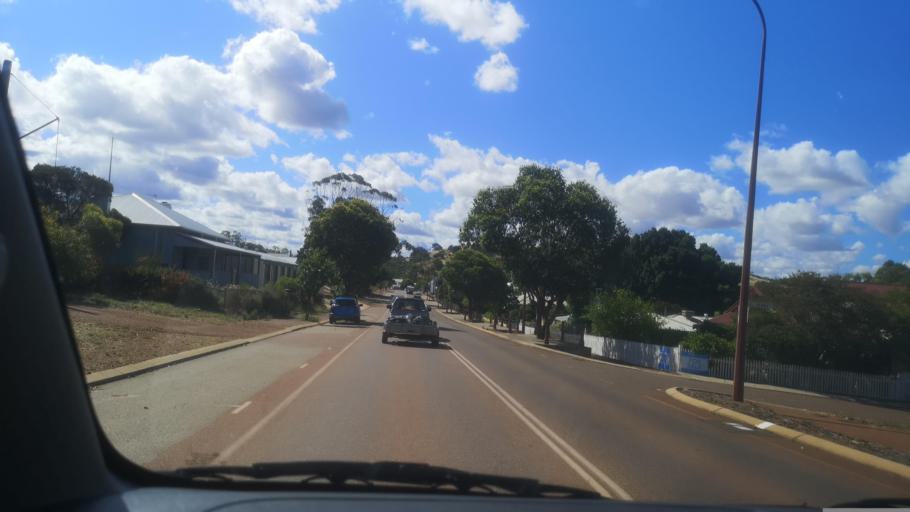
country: AU
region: Western Australia
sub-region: Toodyay
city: Toodyay
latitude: -31.5533
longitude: 116.4726
